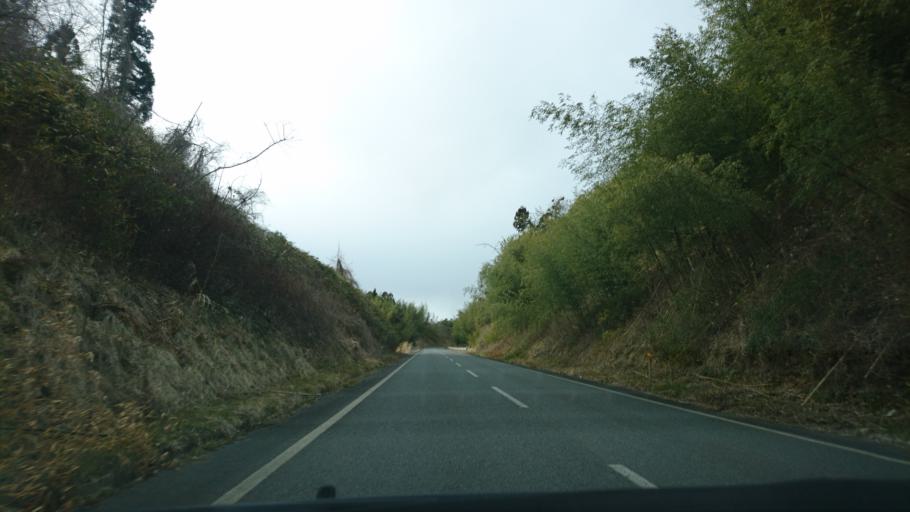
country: JP
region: Iwate
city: Ichinoseki
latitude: 38.8365
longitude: 141.2186
